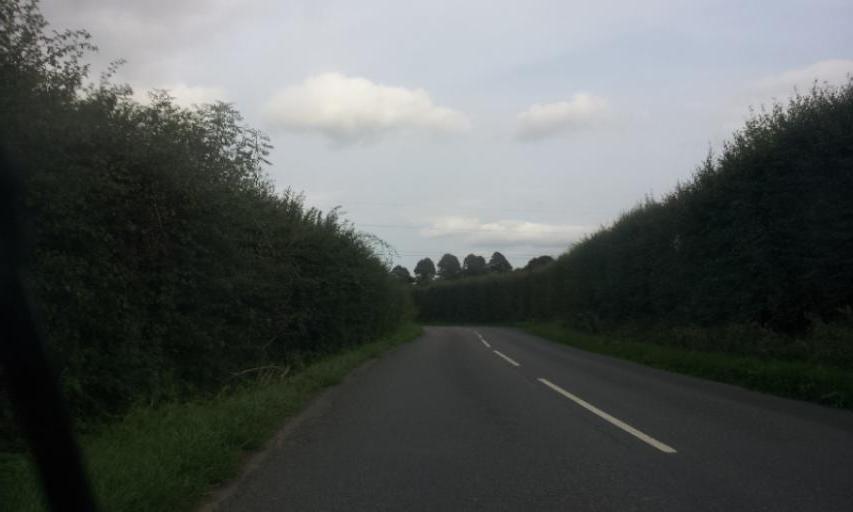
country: GB
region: England
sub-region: Kent
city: Hadlow
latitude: 51.2121
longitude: 0.3268
